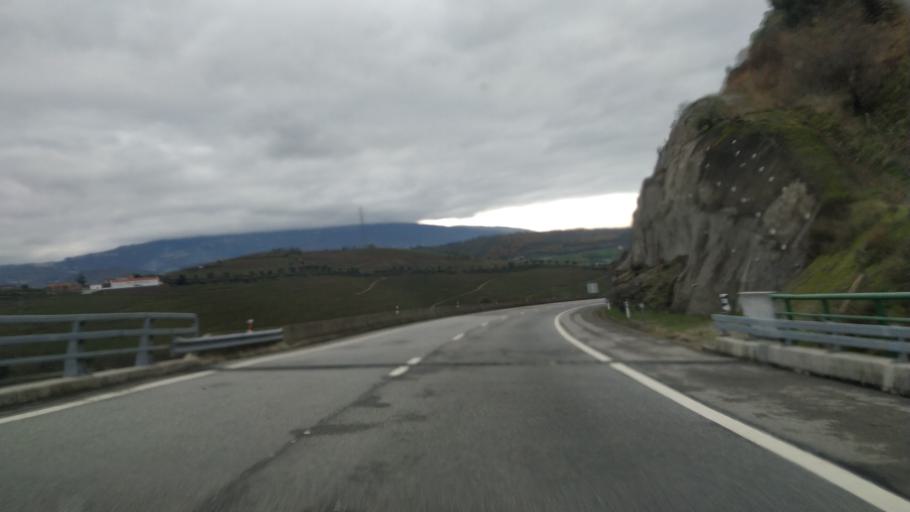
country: PT
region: Vila Real
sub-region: Peso da Regua
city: Peso da Regua
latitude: 41.1731
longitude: -7.7536
